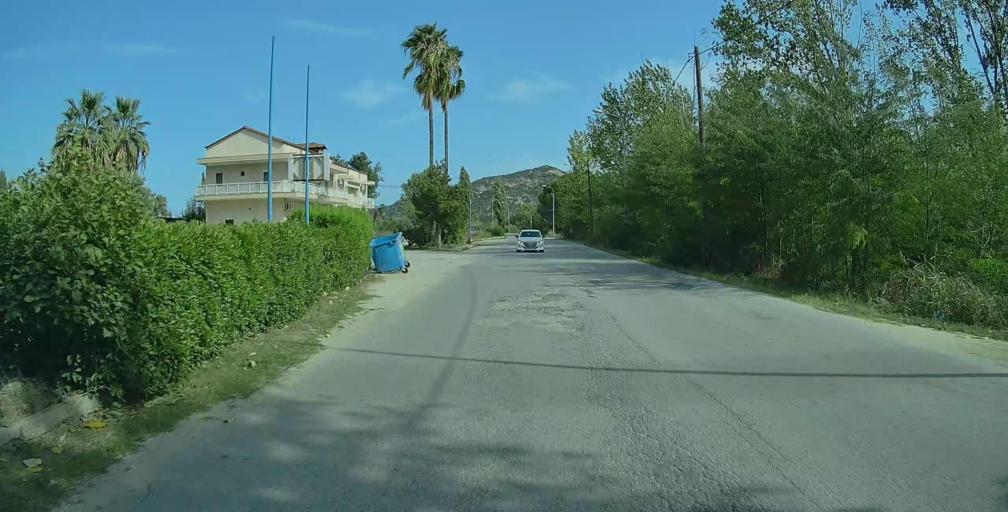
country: GR
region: Central Macedonia
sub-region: Nomos Chalkidikis
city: Sykia
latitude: 40.0345
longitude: 23.9607
